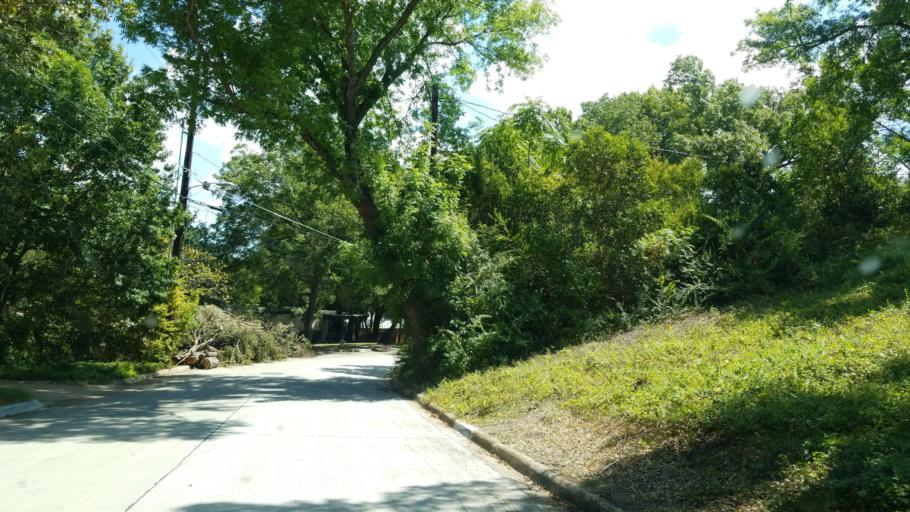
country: US
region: Texas
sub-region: Dallas County
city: Dallas
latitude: 32.7655
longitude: -96.8247
